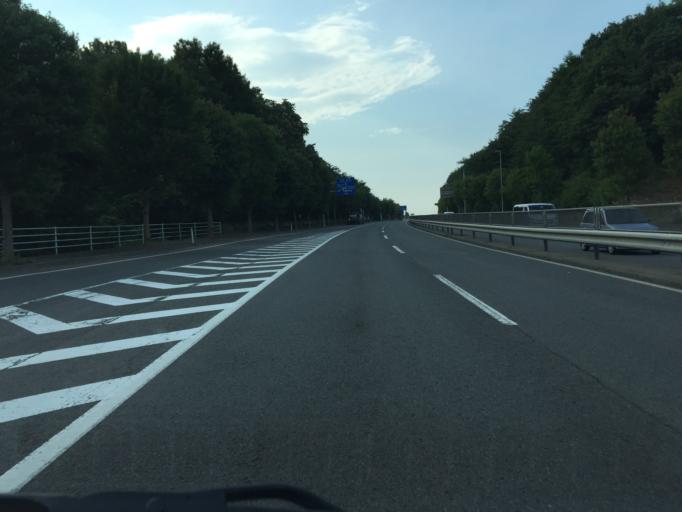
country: JP
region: Fukushima
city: Fukushima-shi
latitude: 37.6899
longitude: 140.4627
